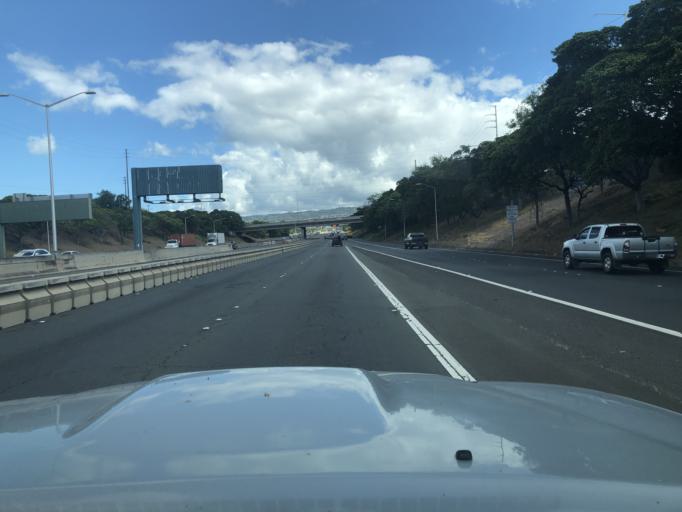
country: US
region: Hawaii
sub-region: Honolulu County
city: Hickam Field
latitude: 21.3496
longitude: -157.9330
